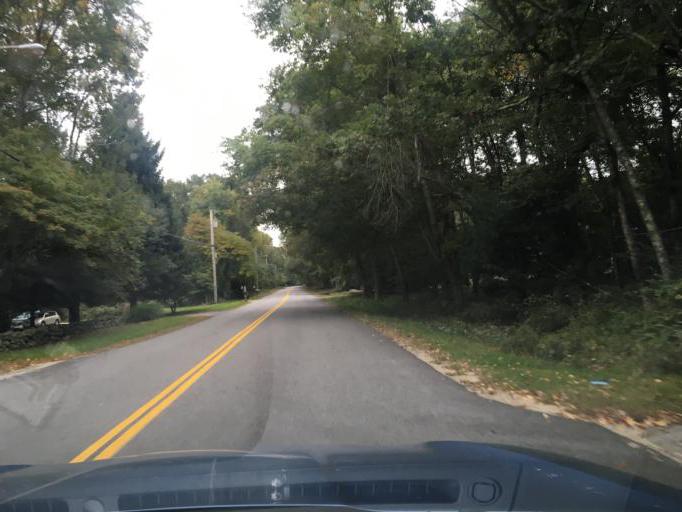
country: US
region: Rhode Island
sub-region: Washington County
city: Exeter
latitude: 41.6156
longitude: -71.5367
